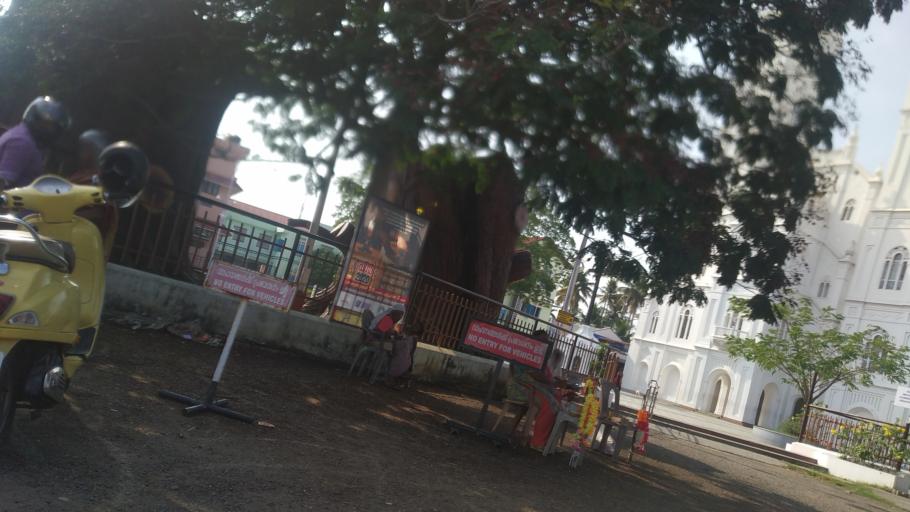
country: IN
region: Kerala
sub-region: Ernakulam
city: Cochin
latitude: 9.9894
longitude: 76.2504
